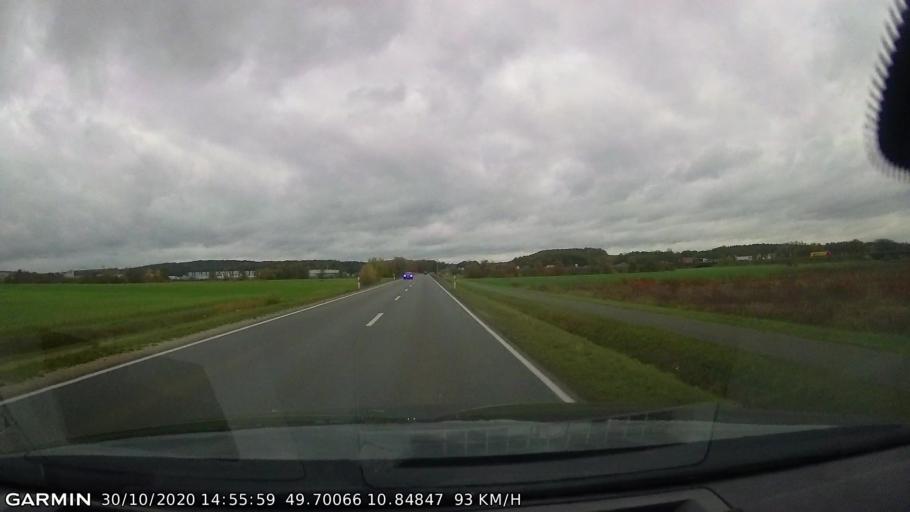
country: DE
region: Bavaria
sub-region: Regierungsbezirk Mittelfranken
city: Gremsdorf
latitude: 49.7007
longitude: 10.8484
